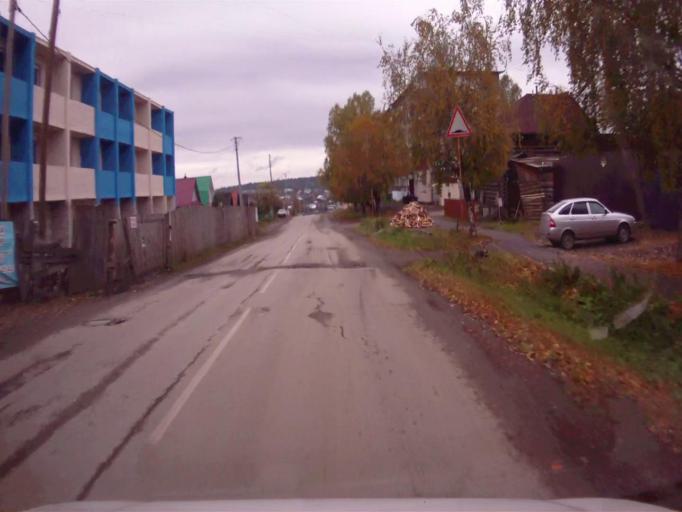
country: RU
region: Chelyabinsk
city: Nyazepetrovsk
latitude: 56.0557
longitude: 59.6056
